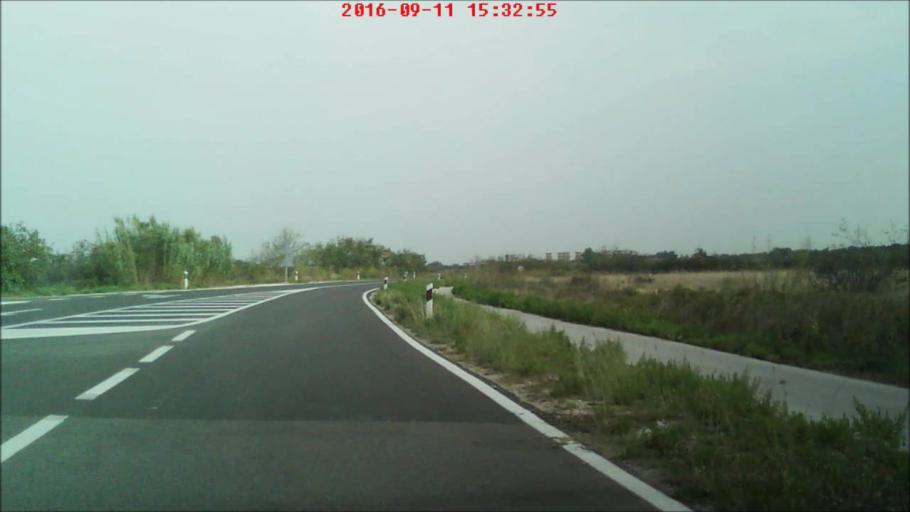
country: HR
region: Zadarska
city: Nin
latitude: 44.2512
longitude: 15.1625
